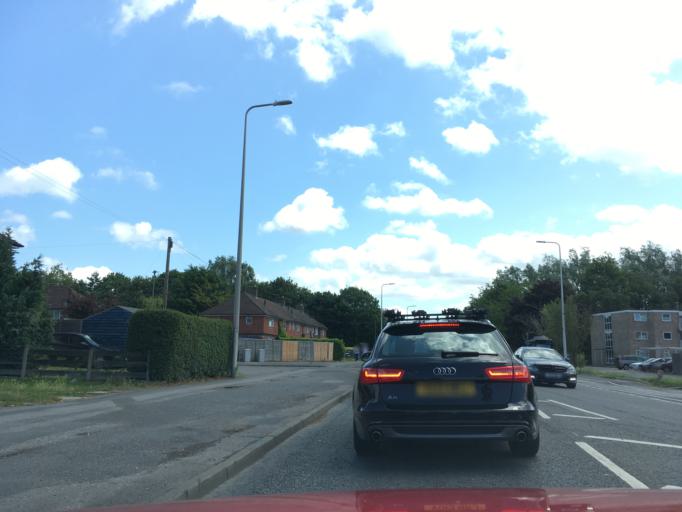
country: GB
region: England
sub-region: West Berkshire
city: Newbury
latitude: 51.4047
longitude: -1.3107
